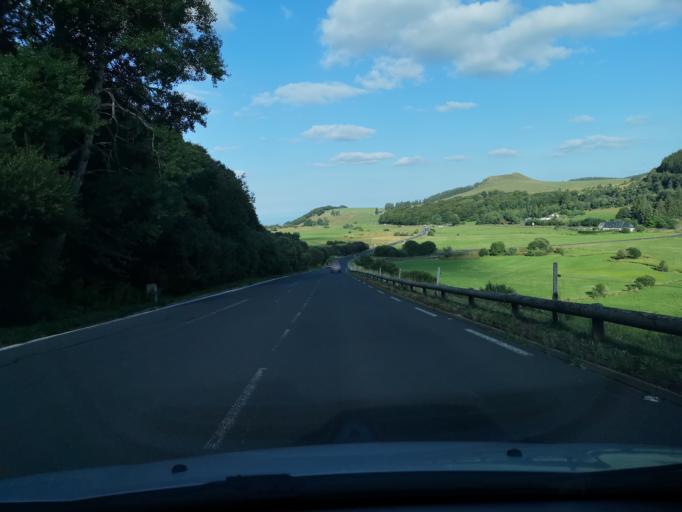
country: FR
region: Auvergne
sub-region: Departement du Puy-de-Dome
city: Mont-Dore
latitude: 45.5031
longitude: 2.8792
